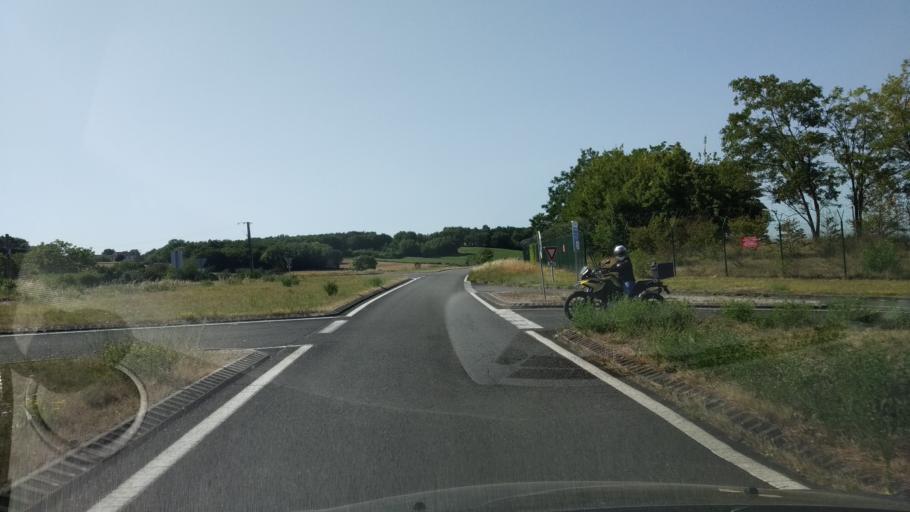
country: FR
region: Poitou-Charentes
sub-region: Departement de la Vienne
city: Lussac-les-Chateaux
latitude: 46.4489
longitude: 0.6504
